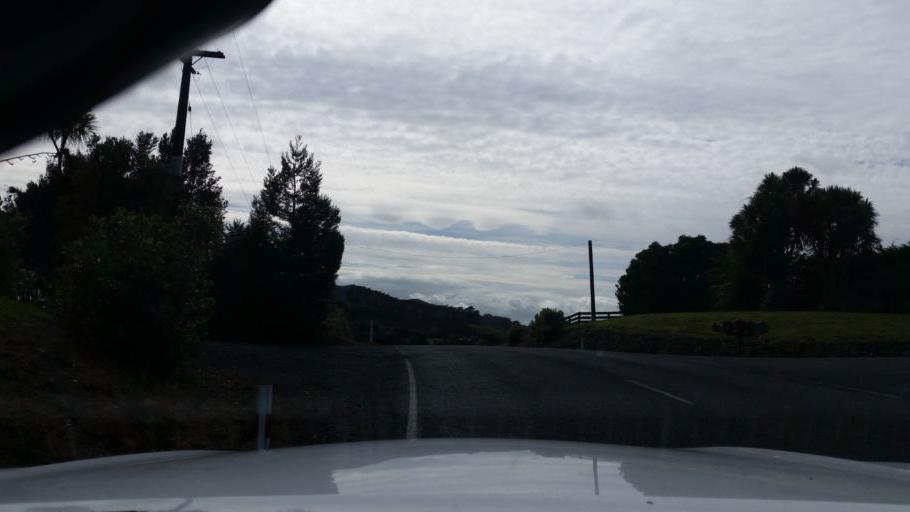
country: NZ
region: Auckland
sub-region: Auckland
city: Wellsford
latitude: -36.0901
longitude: 174.5325
